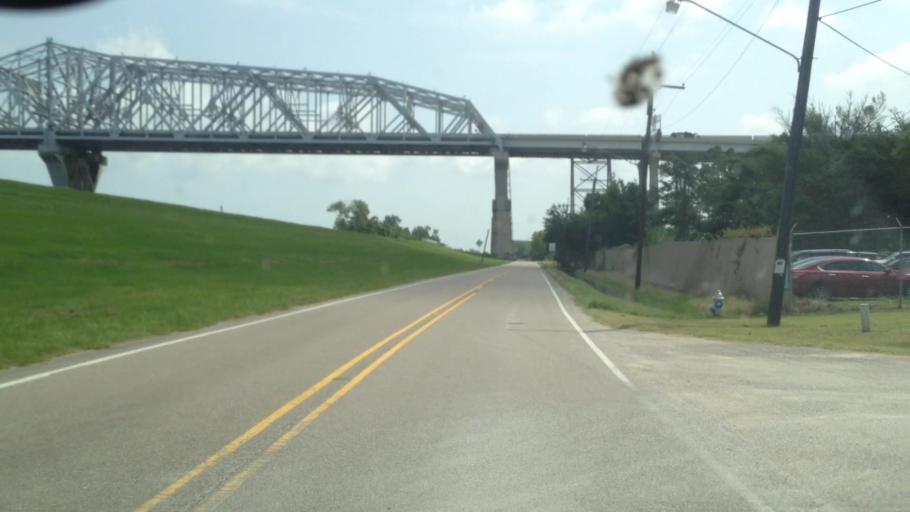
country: US
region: Louisiana
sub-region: Jefferson Parish
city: Bridge City
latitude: 29.9390
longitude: -90.1684
